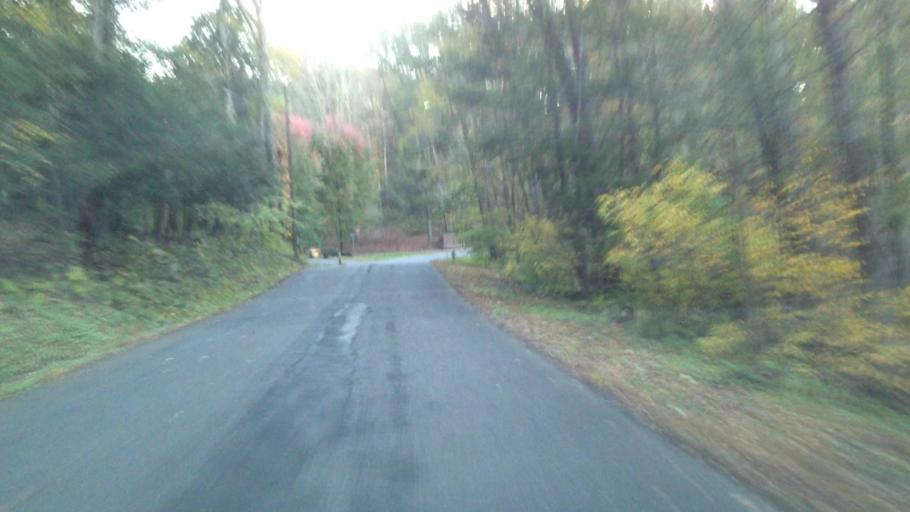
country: US
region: New York
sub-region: Dutchess County
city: Hyde Park
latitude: 41.8085
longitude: -73.9824
